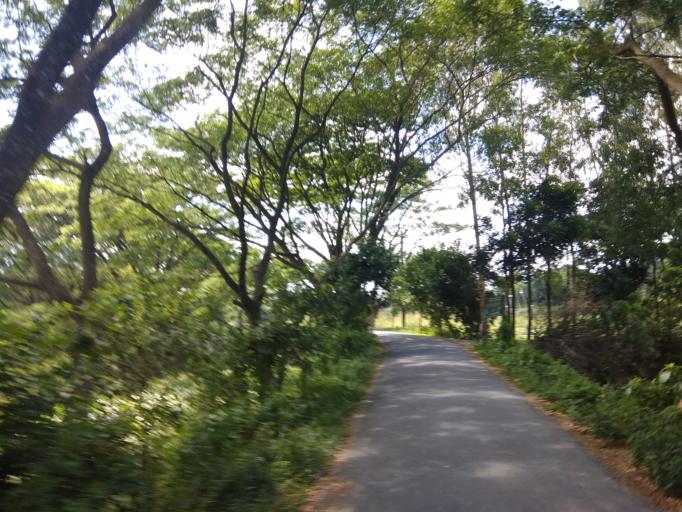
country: BD
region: Dhaka
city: Narayanganj
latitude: 23.4416
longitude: 90.4678
